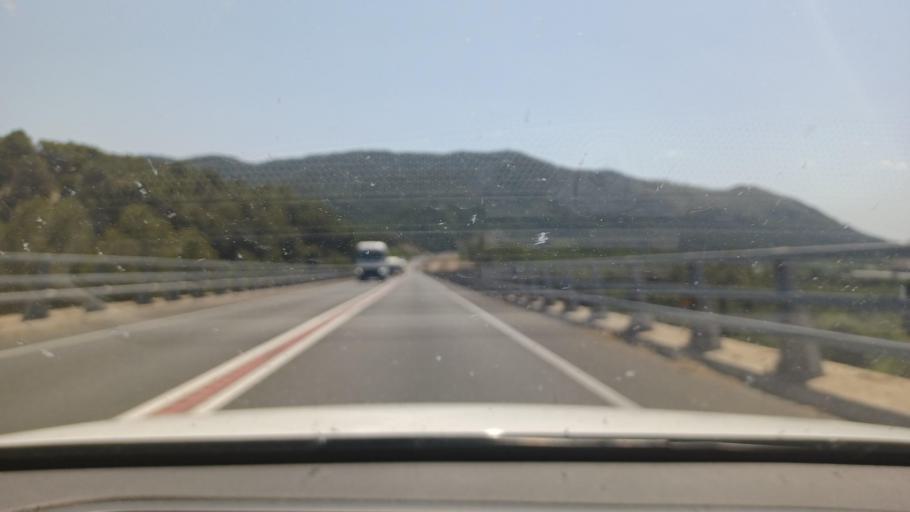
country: ES
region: Catalonia
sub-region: Provincia de Barcelona
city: La Pobla de Claramunt
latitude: 41.5566
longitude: 1.6842
